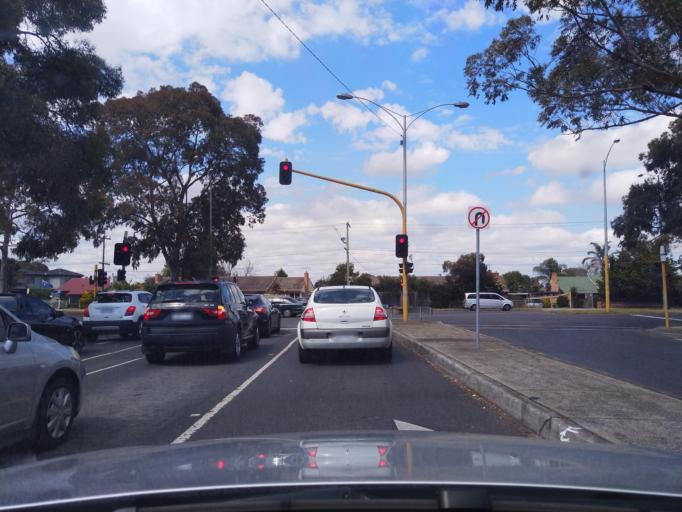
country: AU
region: Victoria
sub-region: Banyule
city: Bellfield
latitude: -37.7494
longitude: 145.0414
